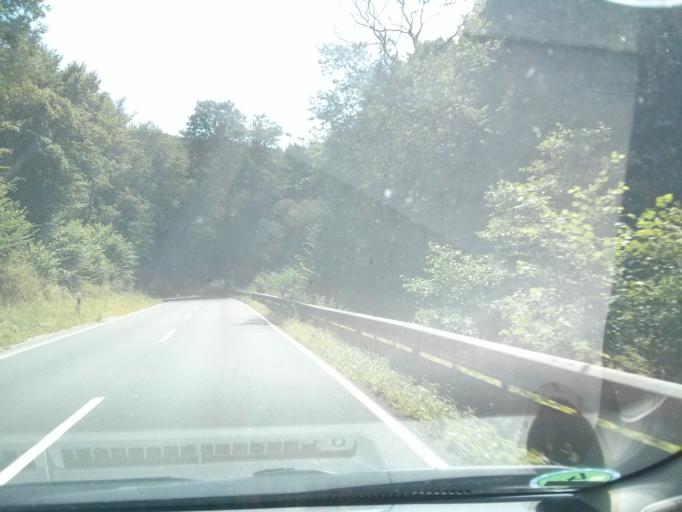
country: DE
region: Rheinland-Pfalz
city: Kalenborn
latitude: 50.5336
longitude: 6.9975
